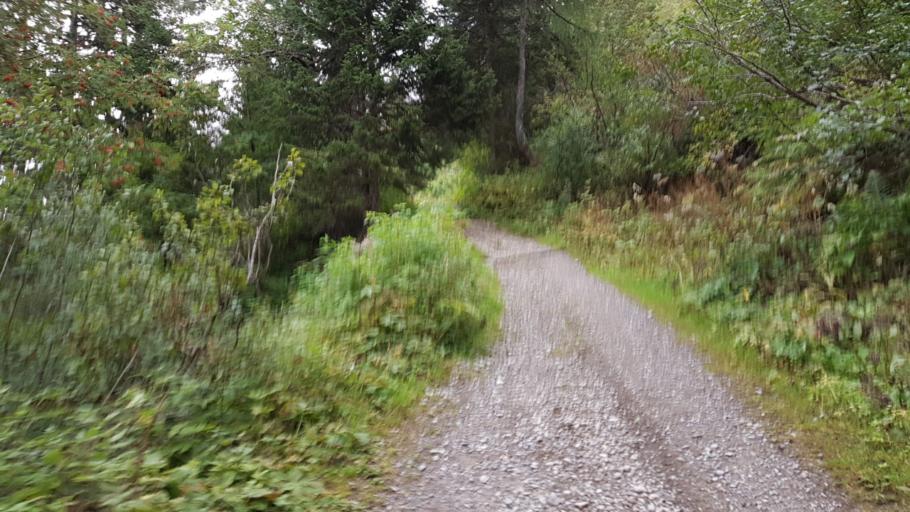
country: CH
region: Bern
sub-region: Frutigen-Niedersimmental District
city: Kandersteg
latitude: 46.4650
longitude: 7.6540
